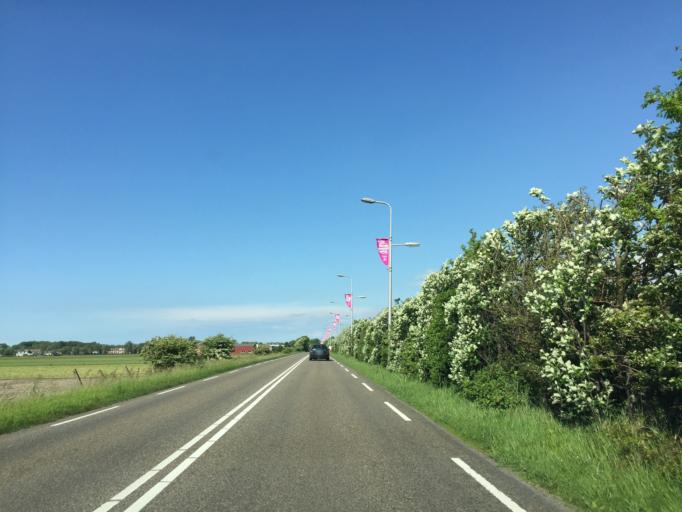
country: NL
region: South Holland
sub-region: Gemeente Noordwijkerhout
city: Noordwijkerhout
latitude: 52.2534
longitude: 4.4784
